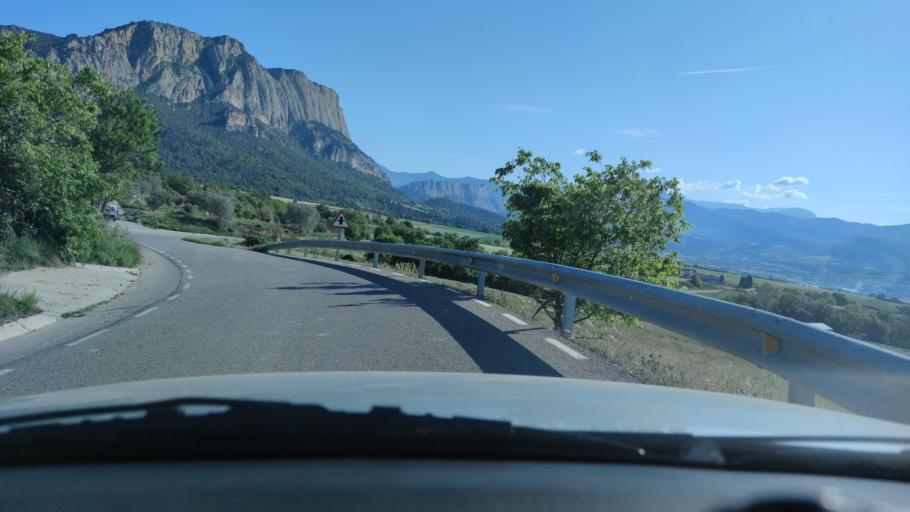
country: ES
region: Catalonia
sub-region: Provincia de Lleida
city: Oliana
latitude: 42.0615
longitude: 1.2743
